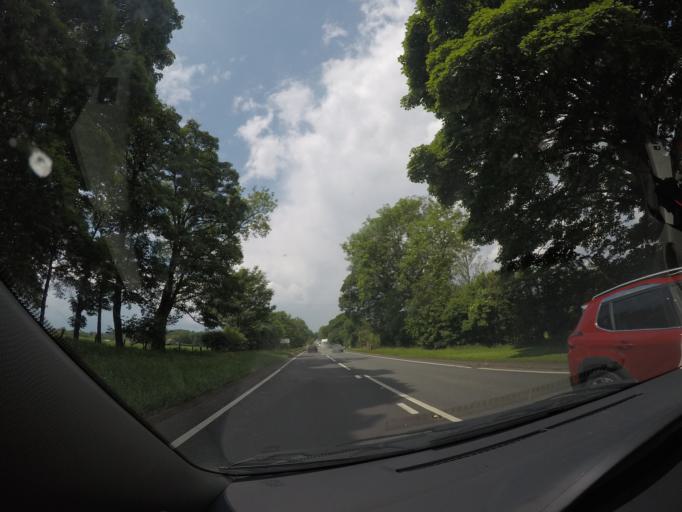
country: GB
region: England
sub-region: Cumbria
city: Kirkby Stephen
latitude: 54.5352
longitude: -2.3760
